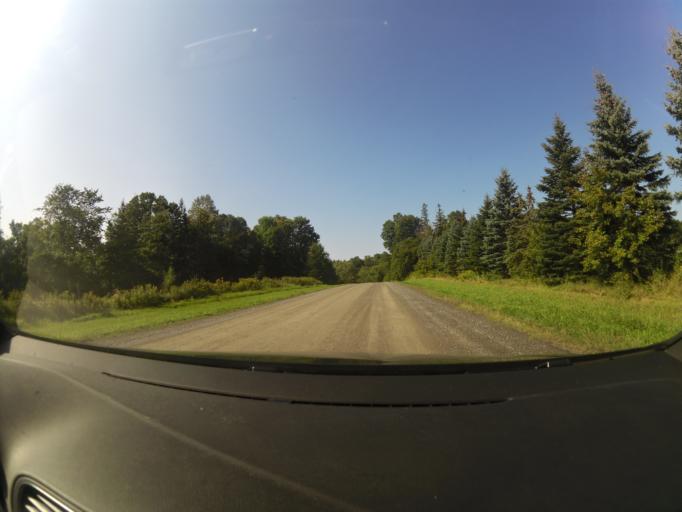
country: CA
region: Ontario
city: Arnprior
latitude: 45.3548
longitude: -76.2606
